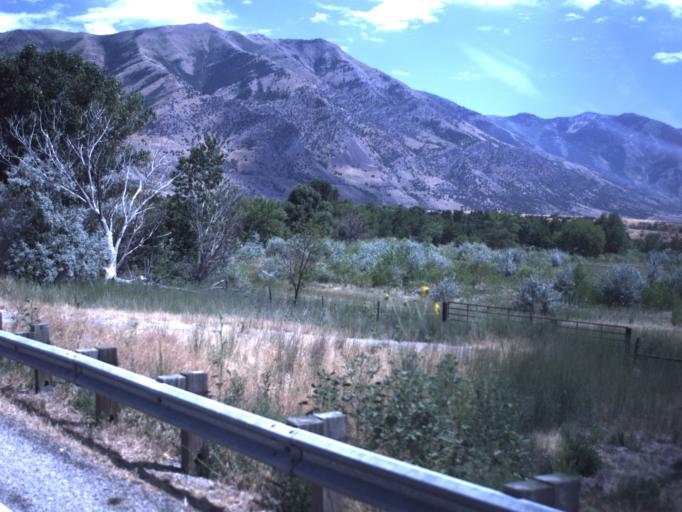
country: US
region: Utah
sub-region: Box Elder County
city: Elwood
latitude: 41.7130
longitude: -112.1188
